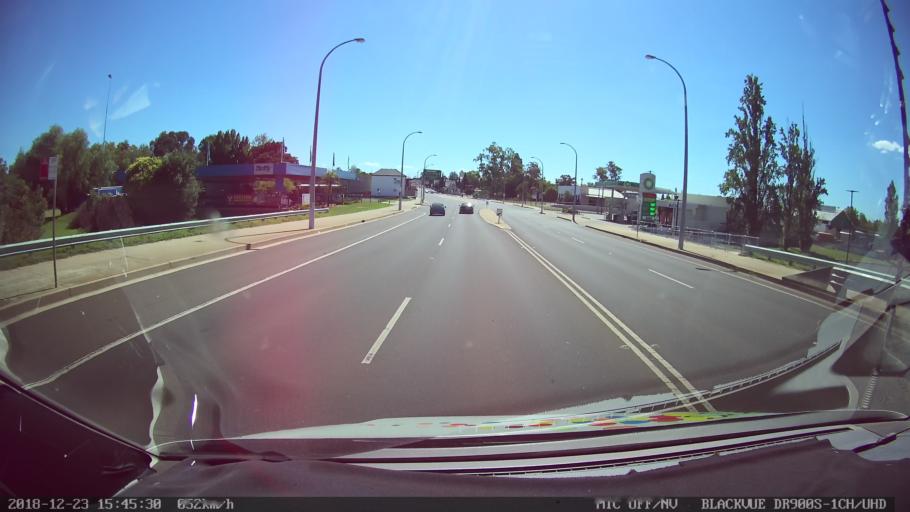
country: AU
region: New South Wales
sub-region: Tamworth Municipality
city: Tamworth
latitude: -31.0914
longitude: 150.9258
